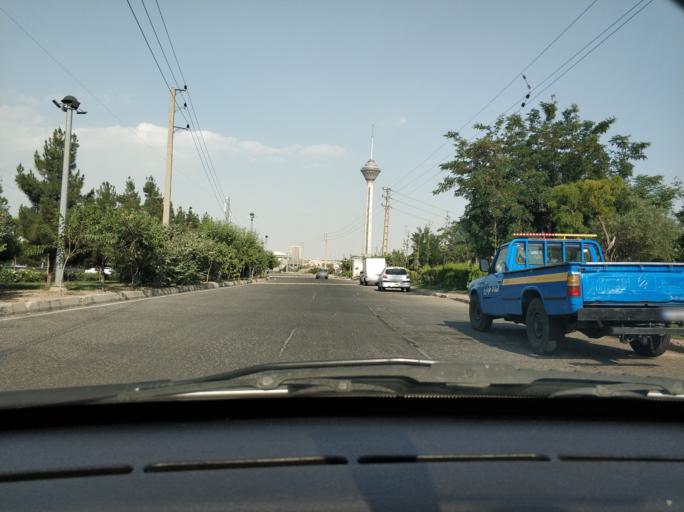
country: IR
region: Tehran
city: Tehran
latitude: 35.7495
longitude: 51.3587
